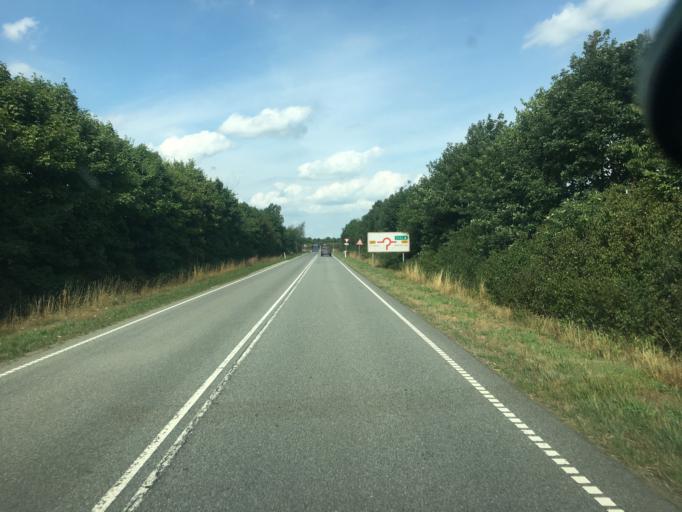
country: DK
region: South Denmark
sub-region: Aabenraa Kommune
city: Tinglev
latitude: 54.9482
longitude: 9.2802
